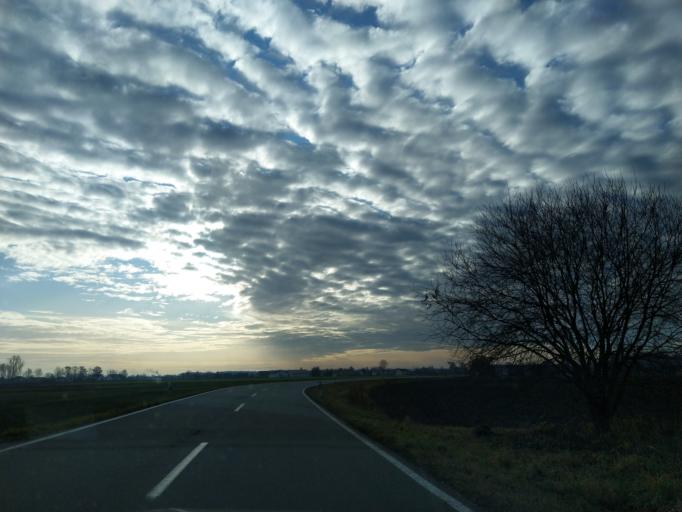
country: DE
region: Bavaria
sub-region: Lower Bavaria
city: Aholming
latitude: 48.7523
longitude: 12.9048
